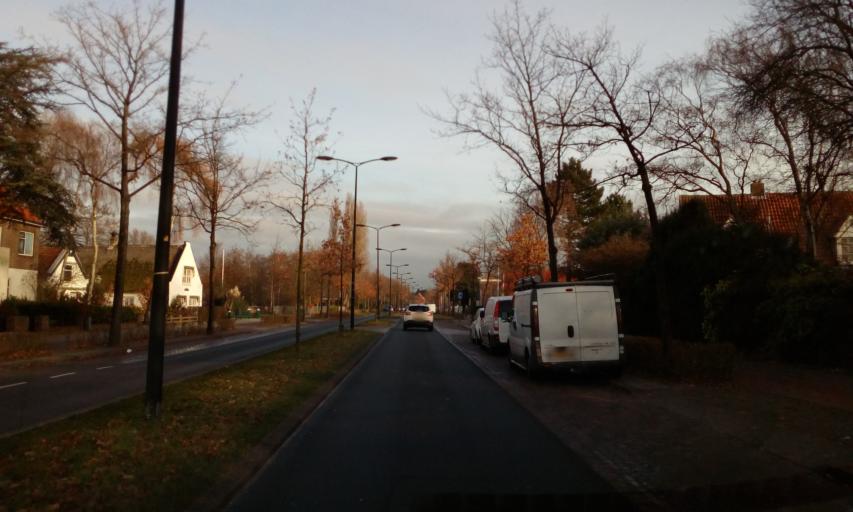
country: NL
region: South Holland
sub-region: Gemeente Voorschoten
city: Voorschoten
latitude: 52.1155
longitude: 4.4346
